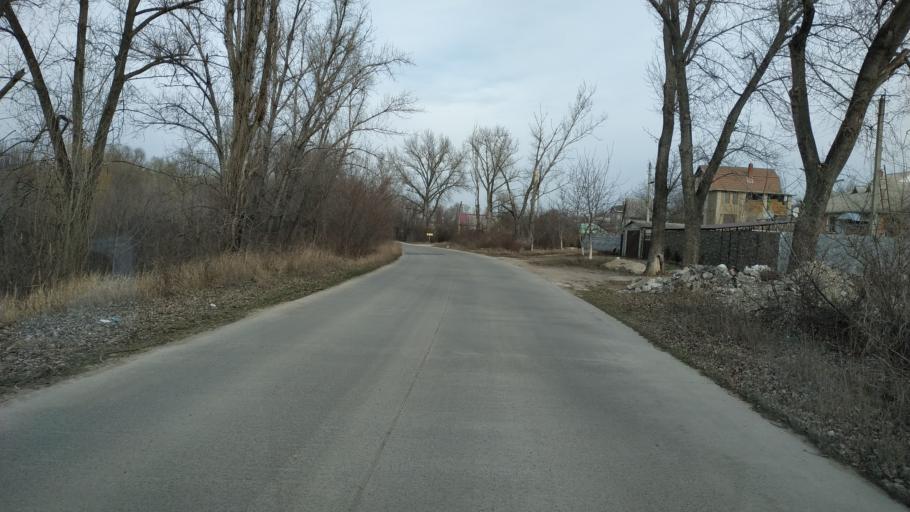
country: MD
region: Chisinau
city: Vatra
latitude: 47.0916
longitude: 28.7389
